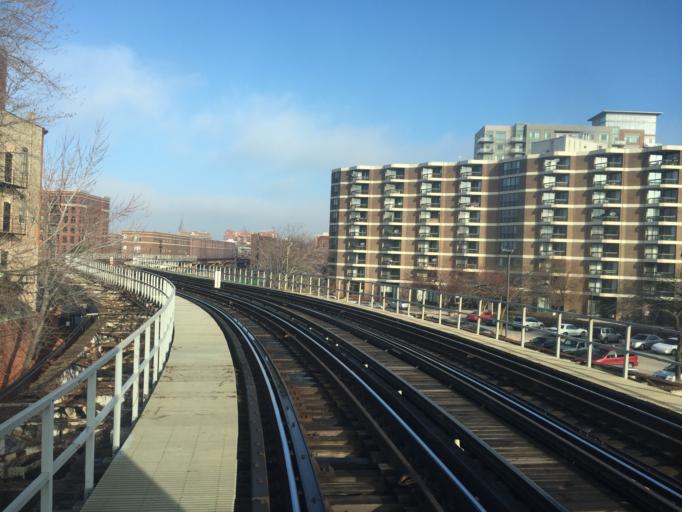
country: US
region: Illinois
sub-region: Cook County
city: Chicago
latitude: 41.9023
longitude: -87.6365
